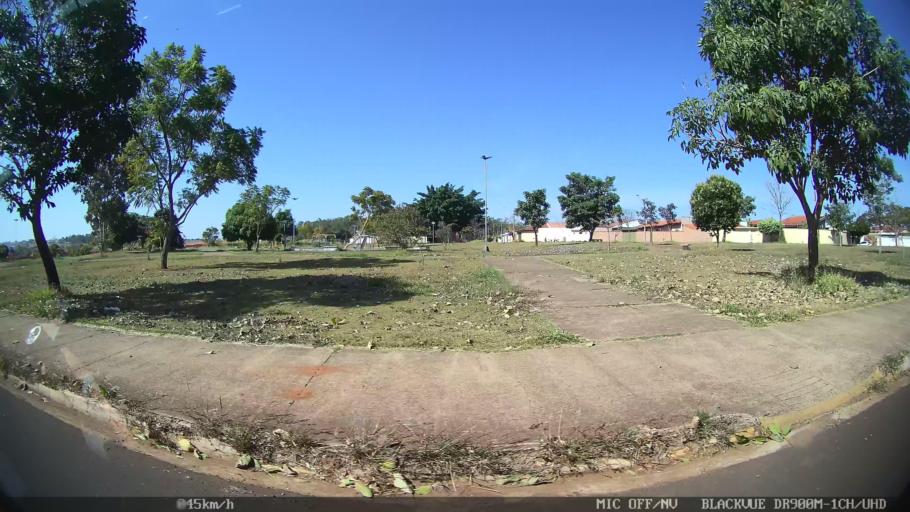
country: BR
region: Sao Paulo
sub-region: Batatais
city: Batatais
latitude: -20.8755
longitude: -47.5940
